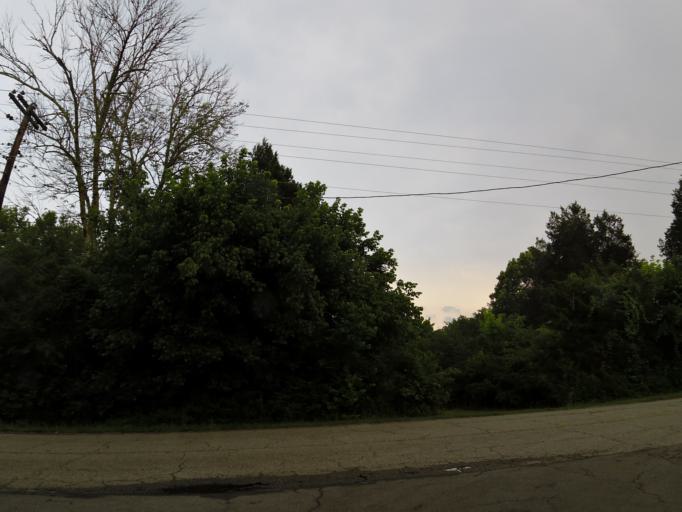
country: US
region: Tennessee
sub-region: Blount County
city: Wildwood
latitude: 35.8077
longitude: -83.7792
